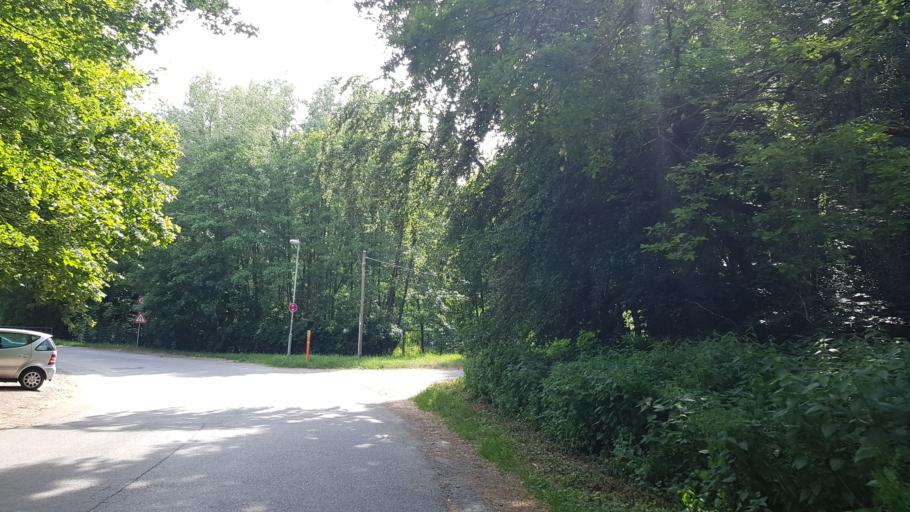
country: DE
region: North Rhine-Westphalia
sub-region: Regierungsbezirk Dusseldorf
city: Muelheim (Ruhr)
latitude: 51.4091
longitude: 6.9243
